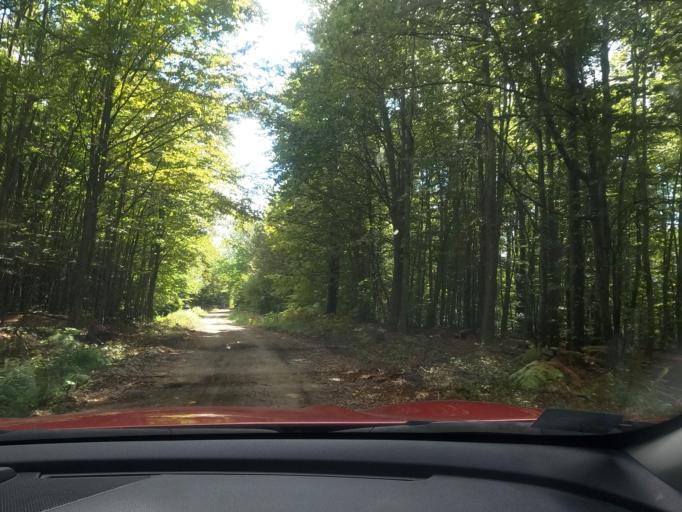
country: BA
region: Federation of Bosnia and Herzegovina
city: Velika Kladusa
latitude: 45.2566
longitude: 15.7895
